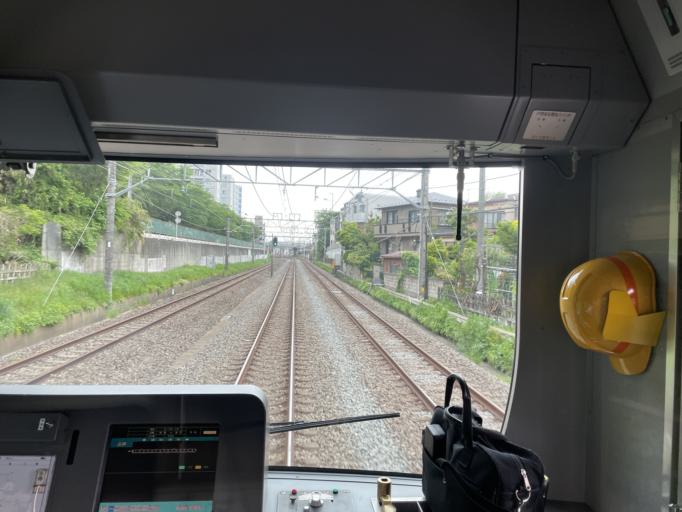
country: JP
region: Saitama
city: Tokorozawa
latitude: 35.7872
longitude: 139.4840
